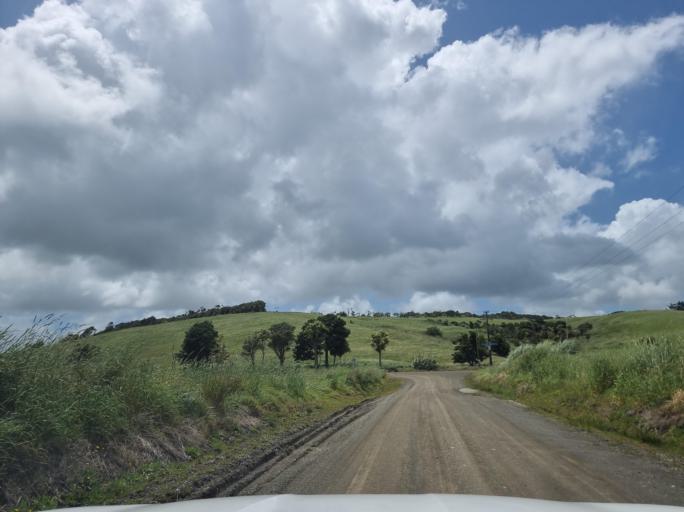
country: NZ
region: Northland
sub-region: Kaipara District
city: Dargaville
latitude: -36.1149
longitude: 174.1320
